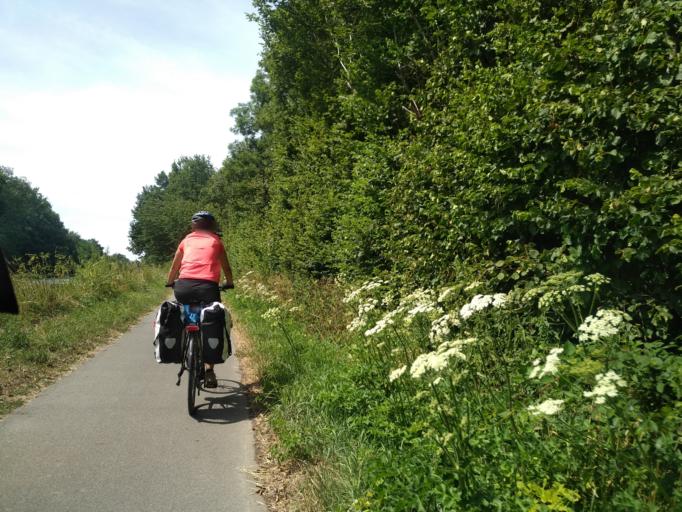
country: FR
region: Auvergne
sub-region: Departement de l'Allier
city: Saint-Francois
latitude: 46.4904
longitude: 3.8491
